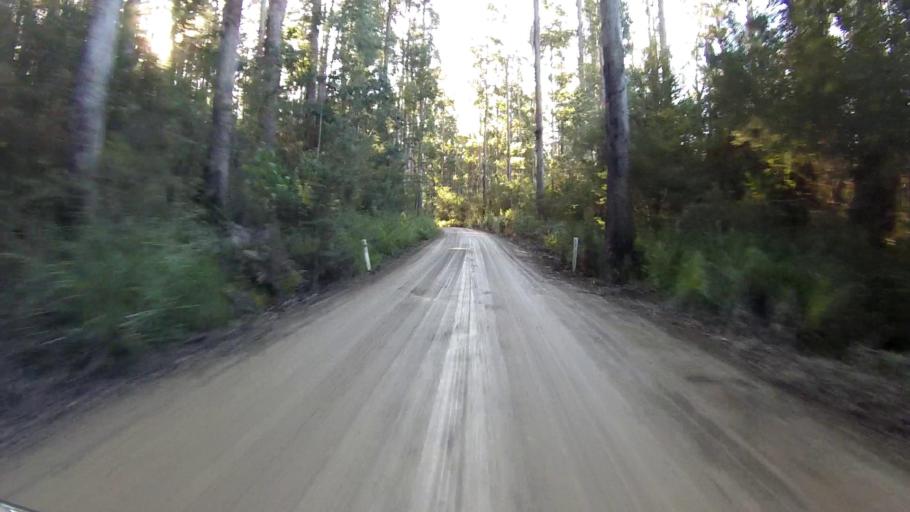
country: AU
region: Tasmania
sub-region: Clarence
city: Sandford
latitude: -43.1260
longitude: 147.9286
